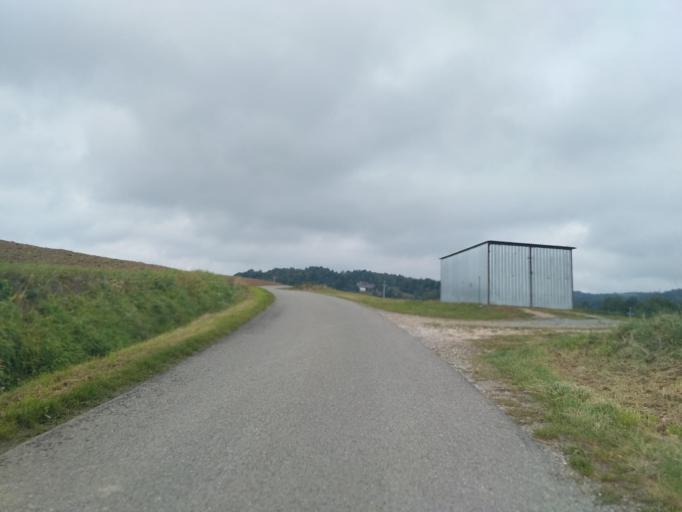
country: PL
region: Subcarpathian Voivodeship
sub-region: Powiat debicki
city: Brzostek
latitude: 49.9394
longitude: 21.4531
